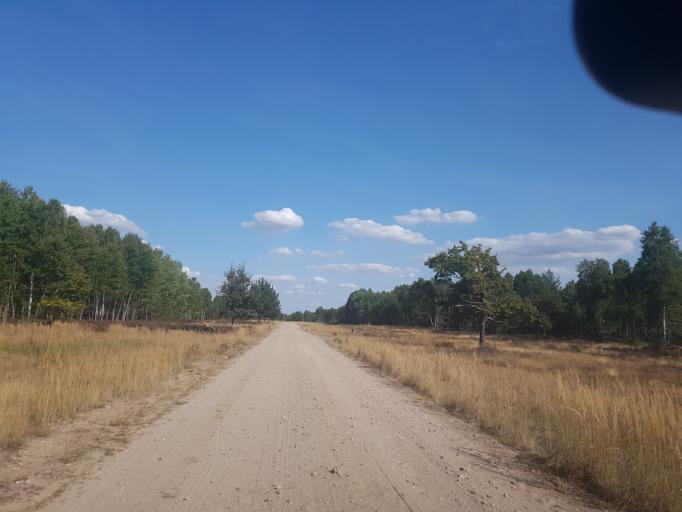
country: DE
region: Saxony-Anhalt
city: Seyda
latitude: 51.8730
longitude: 12.9821
